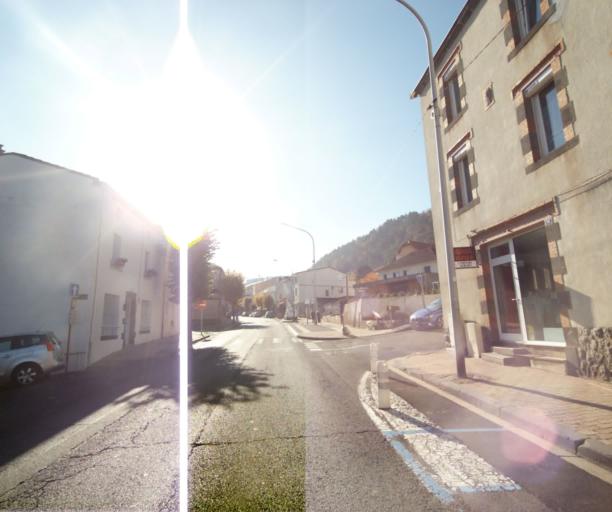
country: FR
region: Auvergne
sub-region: Departement du Puy-de-Dome
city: Ceyrat
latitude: 45.7326
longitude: 3.0638
